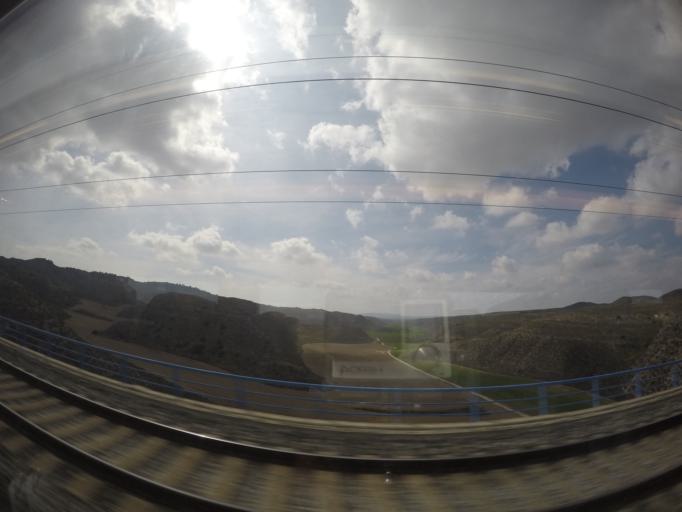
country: ES
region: Aragon
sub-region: Provincia de Zaragoza
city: Monegrillo
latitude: 41.5359
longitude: -0.4192
